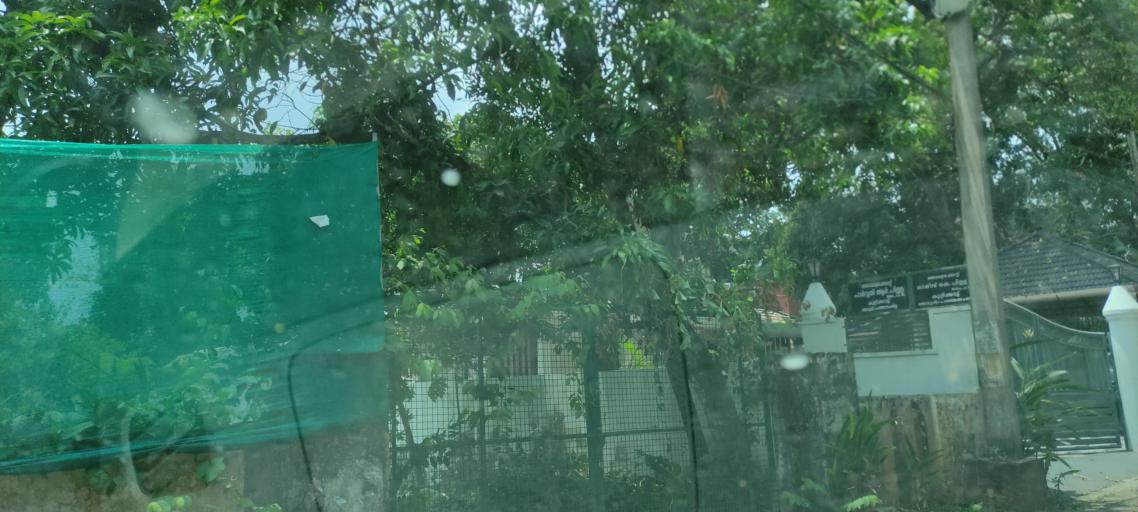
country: IN
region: Kerala
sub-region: Pattanamtitta
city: Adur
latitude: 9.1517
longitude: 76.7302
